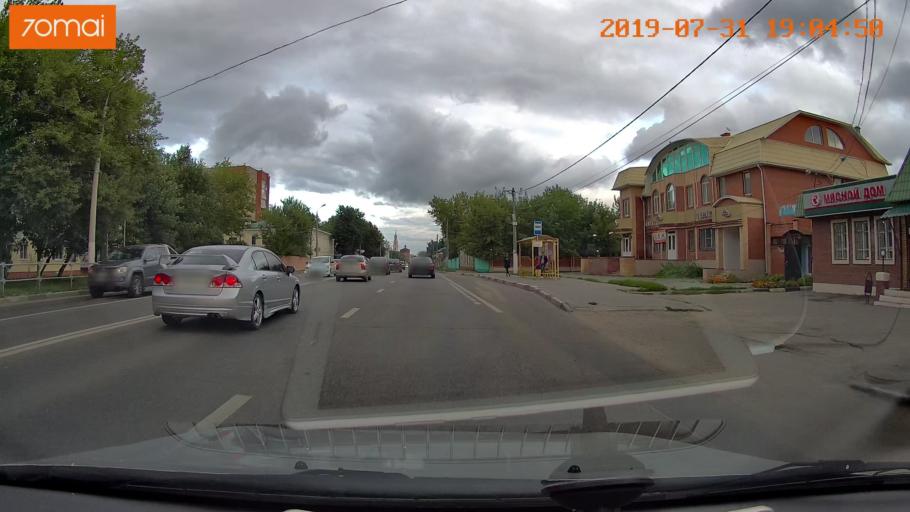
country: RU
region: Moskovskaya
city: Raduzhnyy
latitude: 55.1081
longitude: 38.7424
